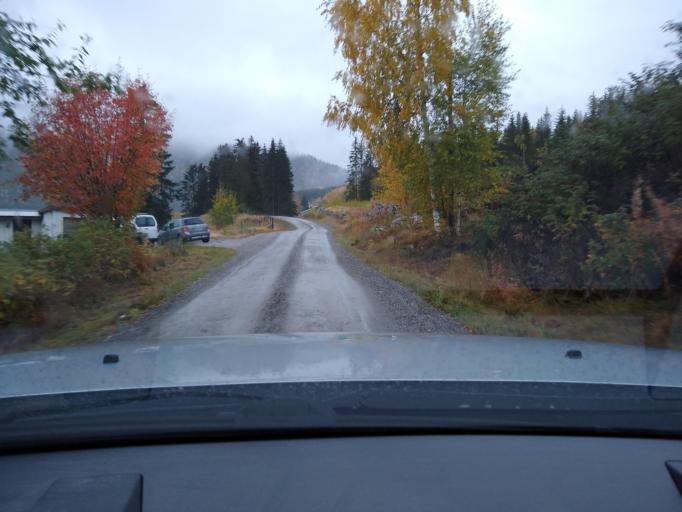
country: NO
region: Oppland
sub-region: Ringebu
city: Ringebu
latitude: 61.5430
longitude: 10.1494
